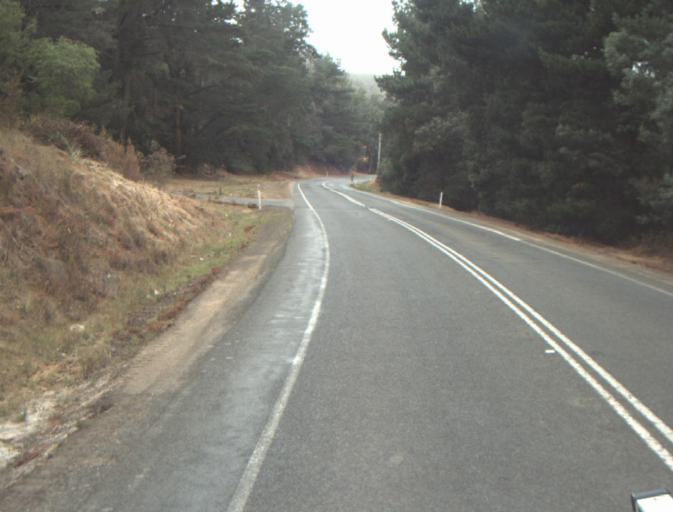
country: AU
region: Tasmania
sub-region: Launceston
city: Mayfield
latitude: -41.2712
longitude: 147.2151
